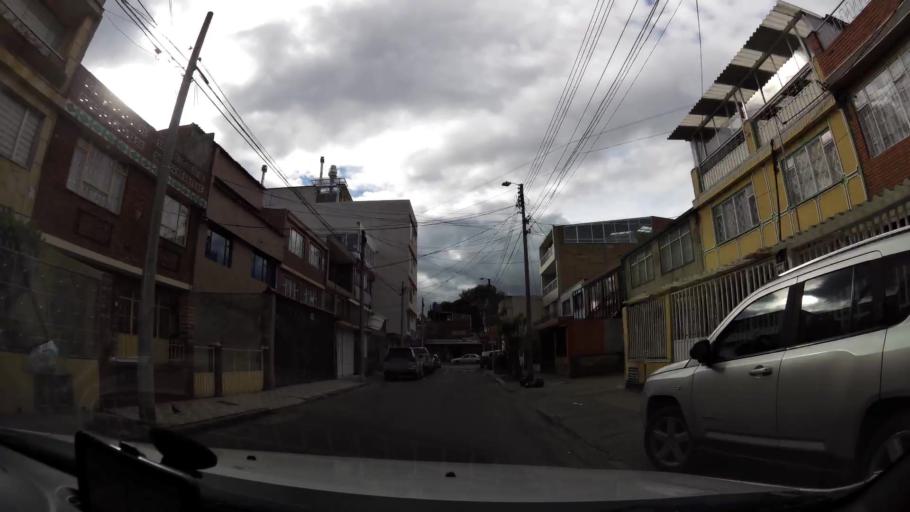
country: CO
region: Bogota D.C.
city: Bogota
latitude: 4.6060
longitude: -74.1249
